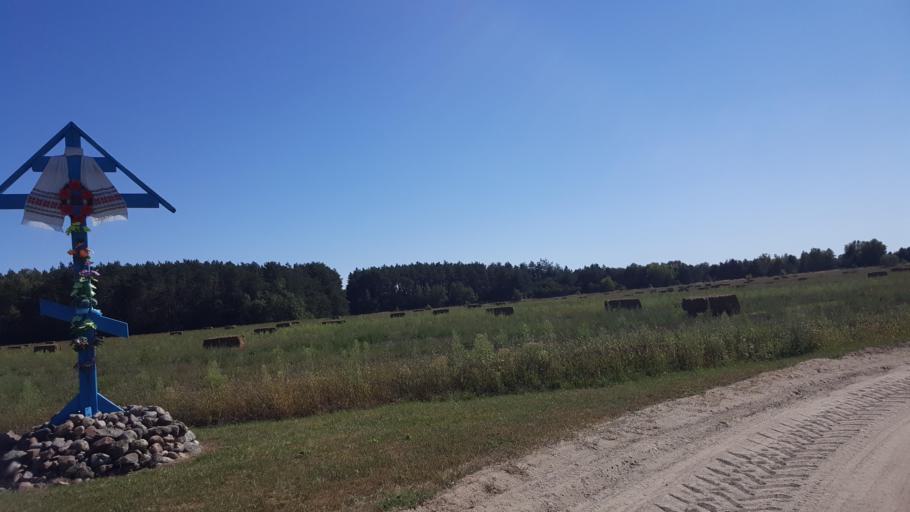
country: PL
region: Lublin Voivodeship
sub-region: Powiat bialski
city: Rokitno
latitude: 52.2179
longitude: 23.3429
